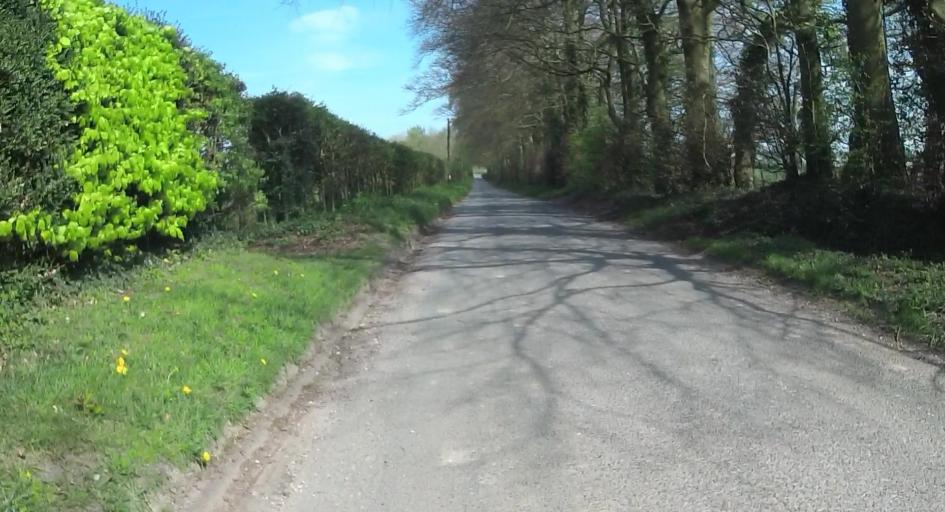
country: GB
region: England
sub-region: Hampshire
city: Basingstoke
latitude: 51.2113
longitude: -1.1529
